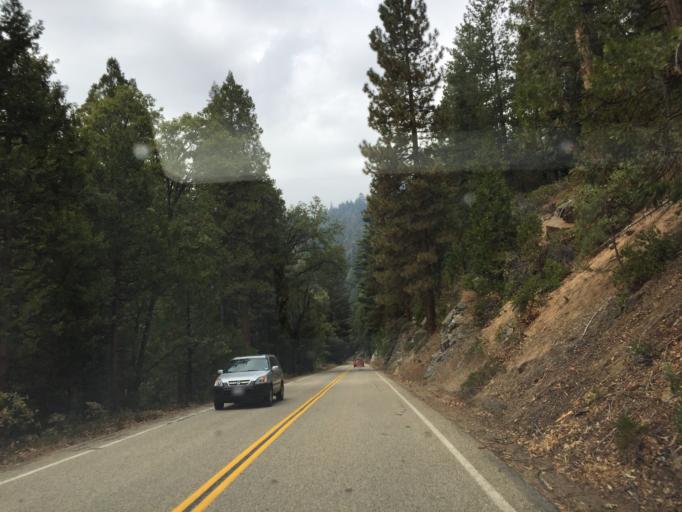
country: US
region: California
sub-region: Tulare County
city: Three Rivers
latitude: 36.7162
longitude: -118.9260
